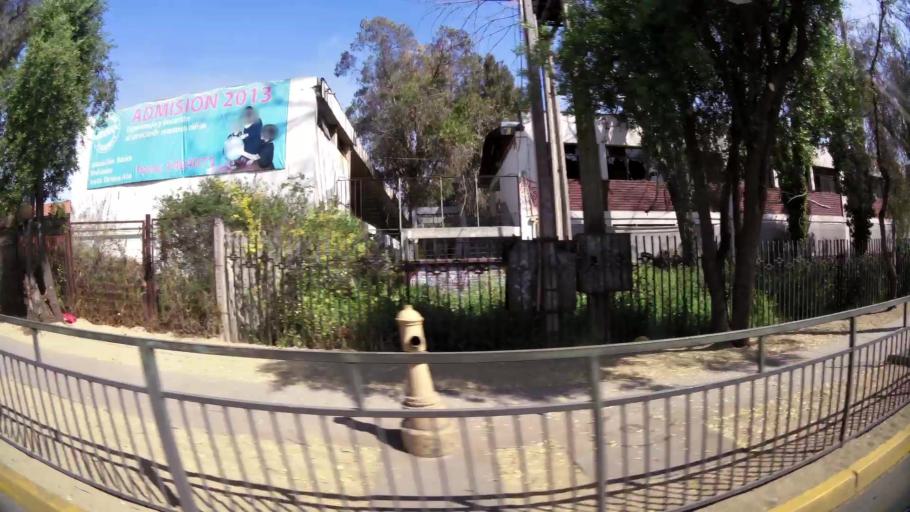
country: CL
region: Santiago Metropolitan
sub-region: Provincia de Santiago
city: La Pintana
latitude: -33.5403
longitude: -70.6513
